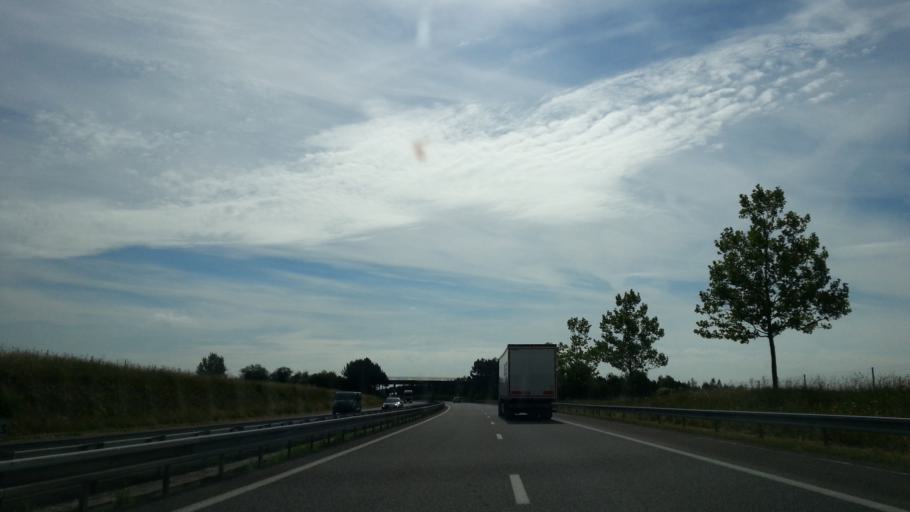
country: FR
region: Champagne-Ardenne
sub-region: Departement de la Marne
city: Fagnieres
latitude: 49.0350
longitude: 4.3570
